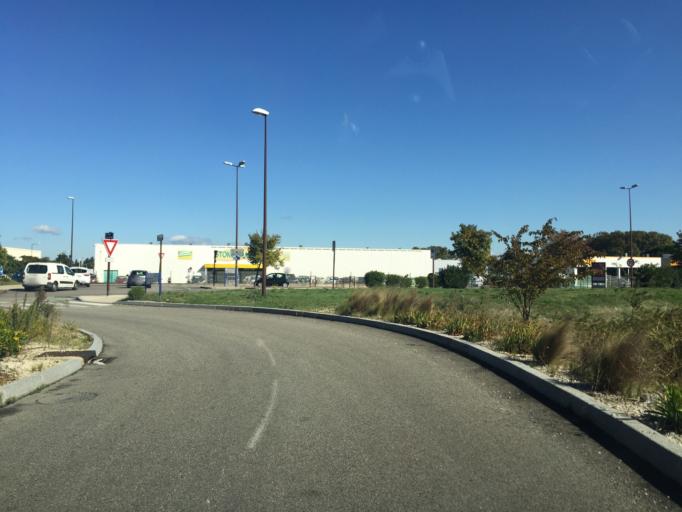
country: FR
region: Provence-Alpes-Cote d'Azur
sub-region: Departement du Vaucluse
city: Montfavet
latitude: 43.9350
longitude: 4.8485
